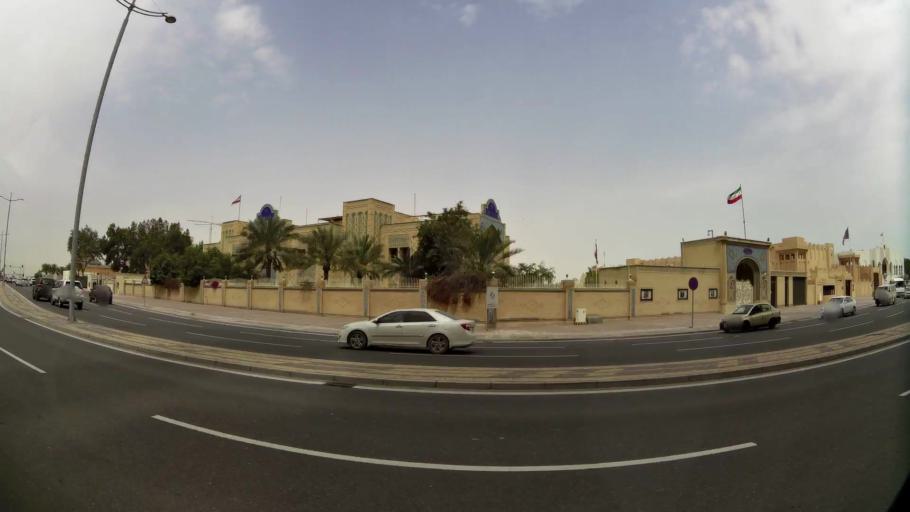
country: QA
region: Baladiyat ad Dawhah
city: Doha
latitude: 25.3303
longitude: 51.5319
